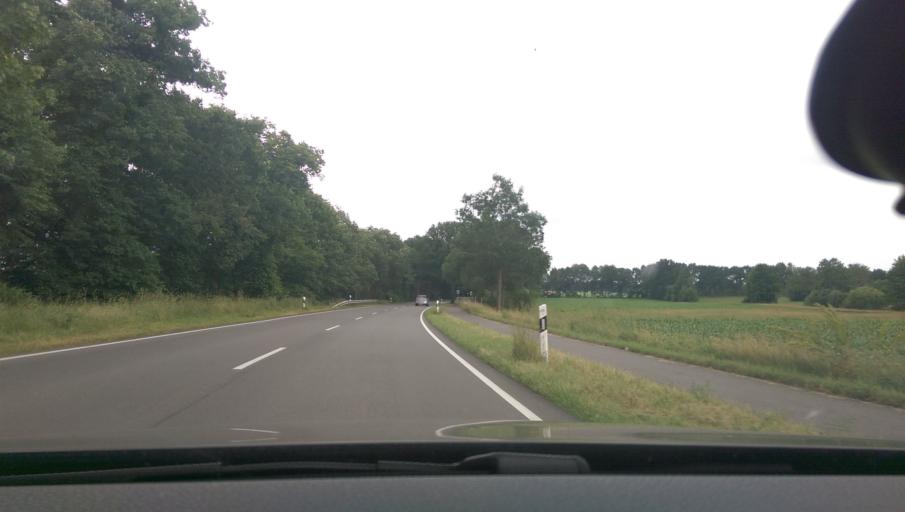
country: DE
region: Lower Saxony
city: Botersen
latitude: 53.1605
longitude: 9.3223
